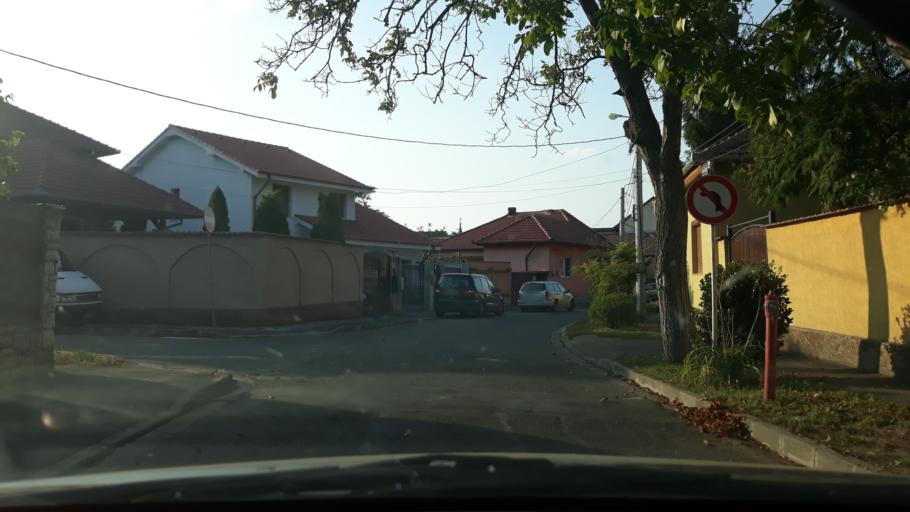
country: RO
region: Bihor
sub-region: Comuna Biharea
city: Oradea
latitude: 47.0473
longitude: 21.9470
